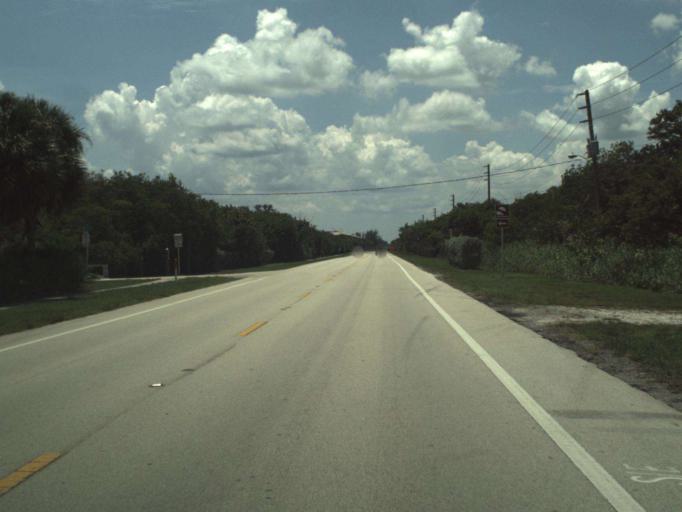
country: US
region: Florida
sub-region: Martin County
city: Jensen Beach
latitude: 27.2444
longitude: -80.1917
